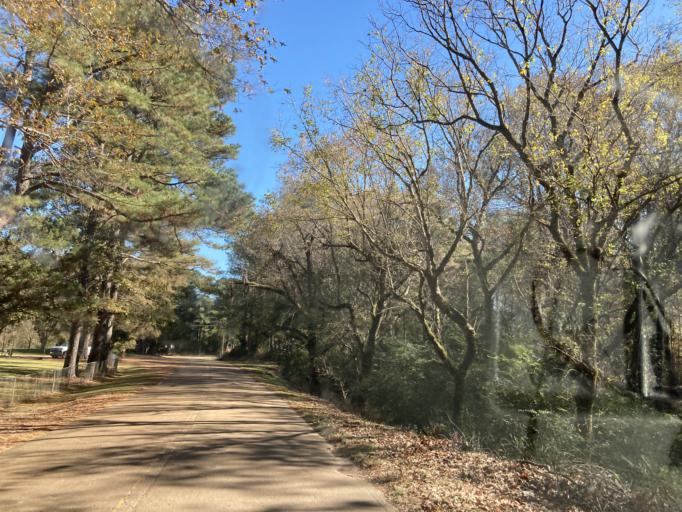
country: US
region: Mississippi
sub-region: Hinds County
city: Lynchburg
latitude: 32.5809
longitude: -90.5656
